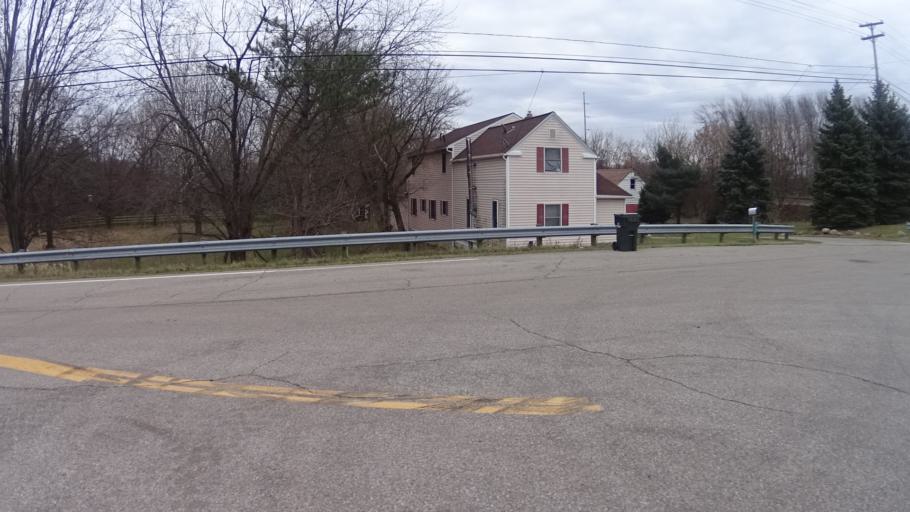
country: US
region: Ohio
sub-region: Lorain County
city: North Ridgeville
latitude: 41.3761
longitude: -82.0189
